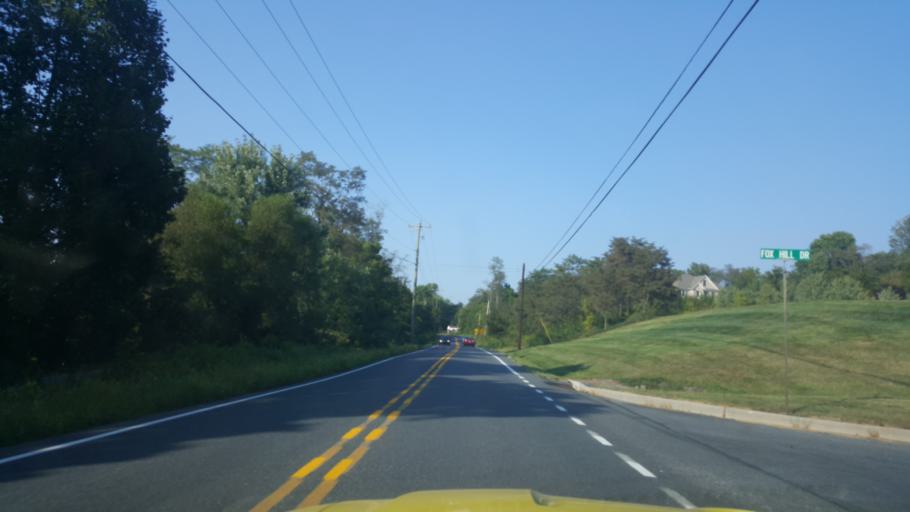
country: US
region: Pennsylvania
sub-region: Lebanon County
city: Campbelltown
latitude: 40.2262
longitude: -76.5353
